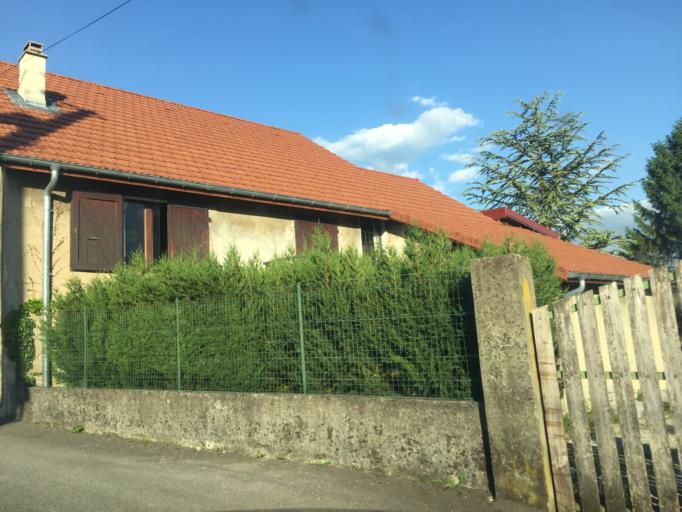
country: FR
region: Rhone-Alpes
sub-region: Departement de la Savoie
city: Les Marches
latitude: 45.5100
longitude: 5.9809
